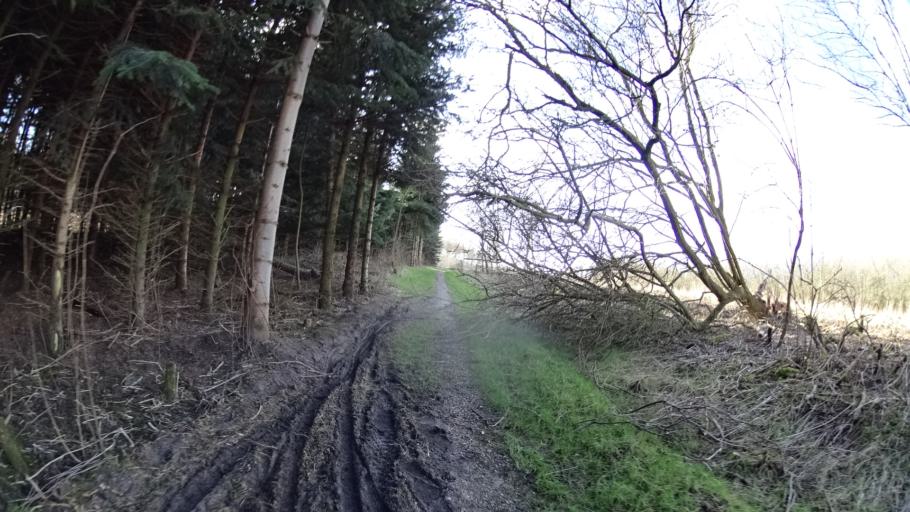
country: DK
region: Central Jutland
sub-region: Arhus Kommune
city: Tranbjerg
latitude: 56.1062
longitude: 10.1236
